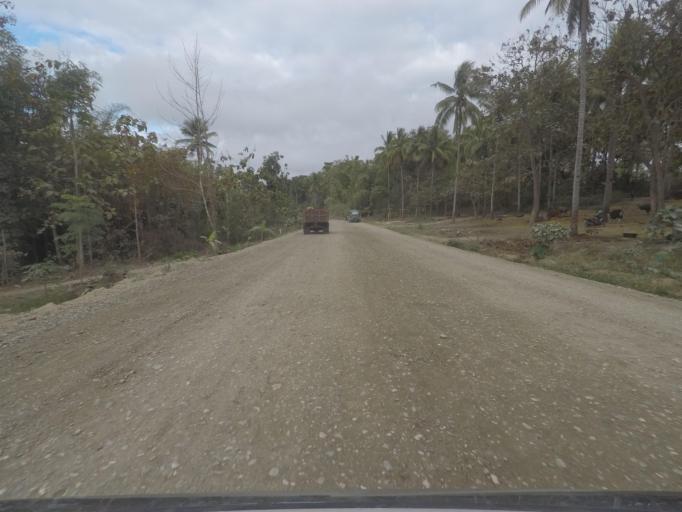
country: TL
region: Baucau
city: Baucau
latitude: -8.4962
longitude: 126.4540
